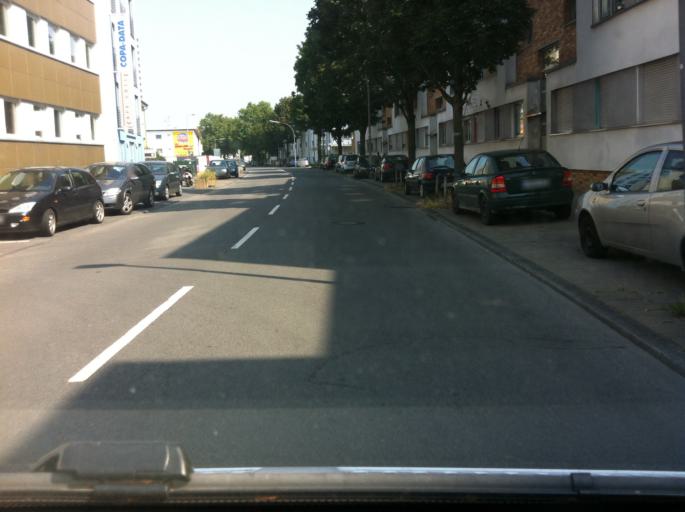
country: DE
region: North Rhine-Westphalia
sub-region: Regierungsbezirk Koln
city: Bilderstoeckchen
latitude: 50.9546
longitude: 6.8993
